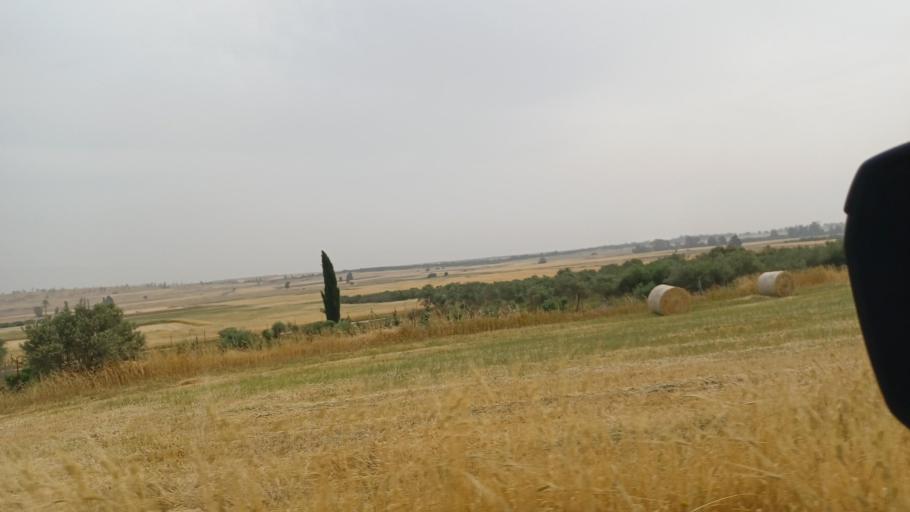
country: CY
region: Lefkosia
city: Mammari
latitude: 35.1764
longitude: 33.2154
